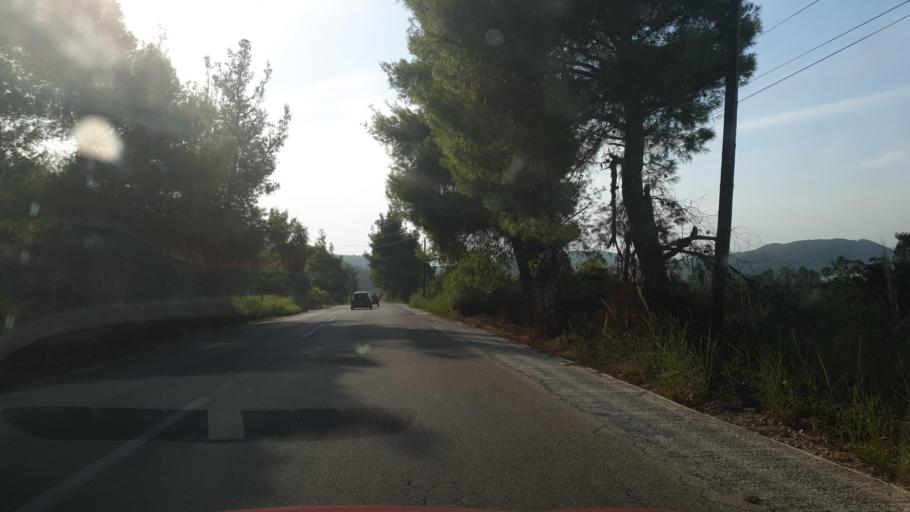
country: GR
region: Central Macedonia
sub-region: Nomos Chalkidikis
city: Neos Marmaras
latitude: 40.1836
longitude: 23.7890
